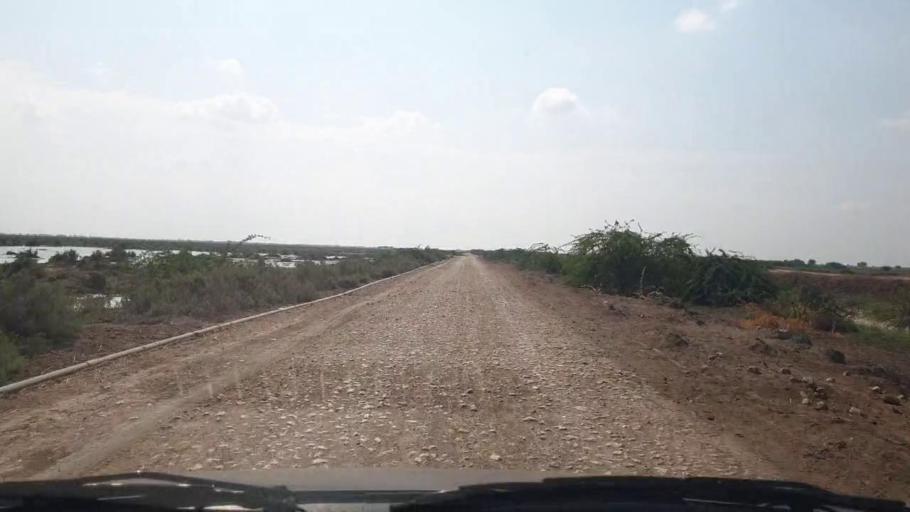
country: PK
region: Sindh
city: Badin
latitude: 24.5083
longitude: 68.6081
